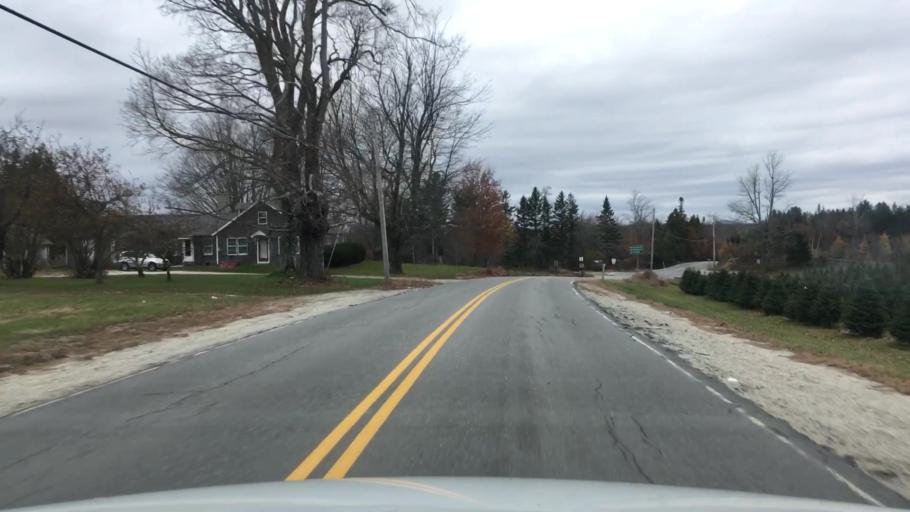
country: US
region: Maine
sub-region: Hancock County
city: Penobscot
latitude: 44.4417
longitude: -68.6361
